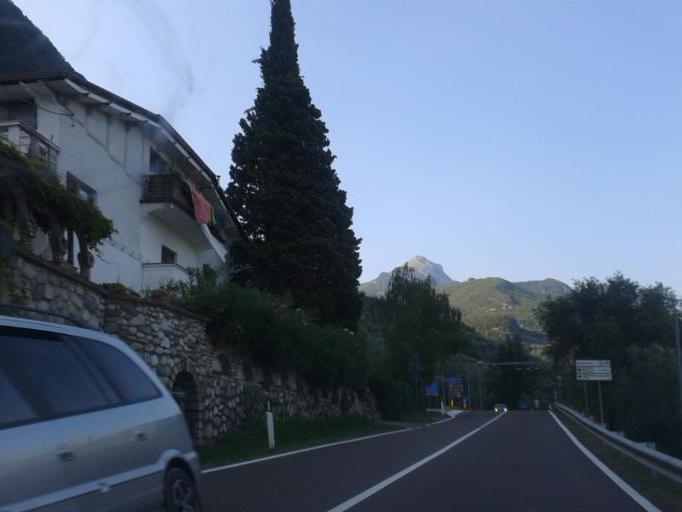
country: IT
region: Trentino-Alto Adige
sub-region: Provincia di Trento
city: Riva del Garda
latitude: 45.9018
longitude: 10.8339
